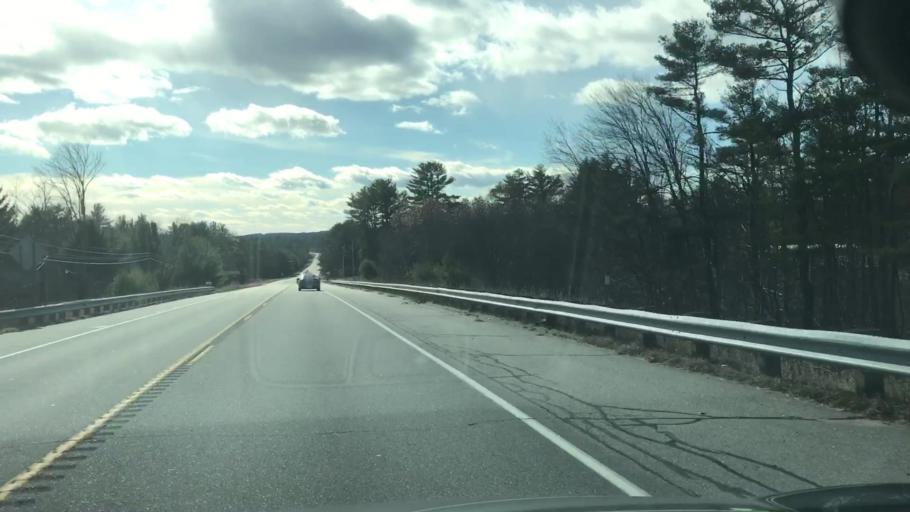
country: US
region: New Hampshire
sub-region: Merrimack County
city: Pittsfield
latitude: 43.2844
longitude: -71.3612
